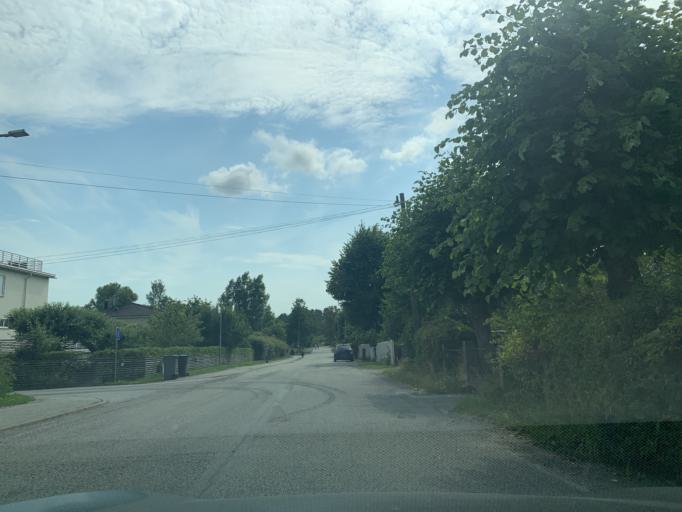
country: SE
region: Stockholm
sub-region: Norrtalje Kommun
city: Bergshamra
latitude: 59.4009
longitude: 18.0168
